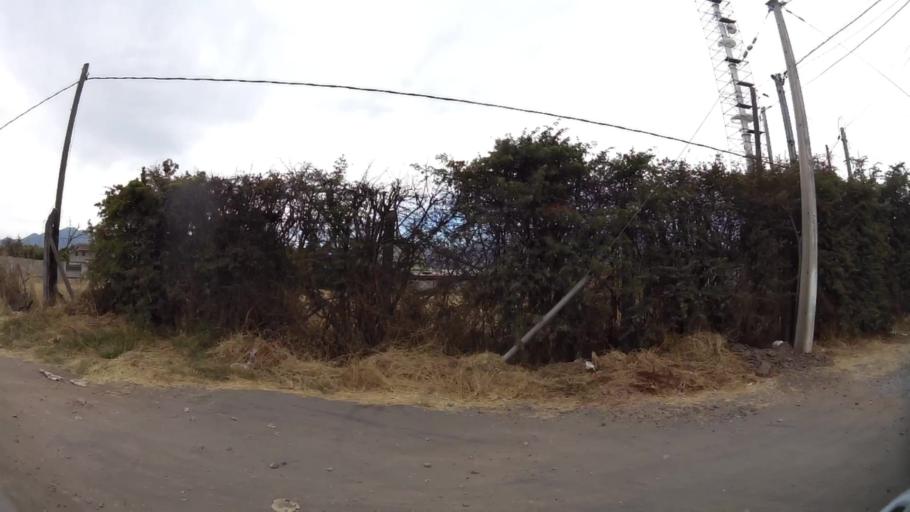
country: CL
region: O'Higgins
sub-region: Provincia de Cachapoal
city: Rancagua
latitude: -34.1284
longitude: -70.7332
